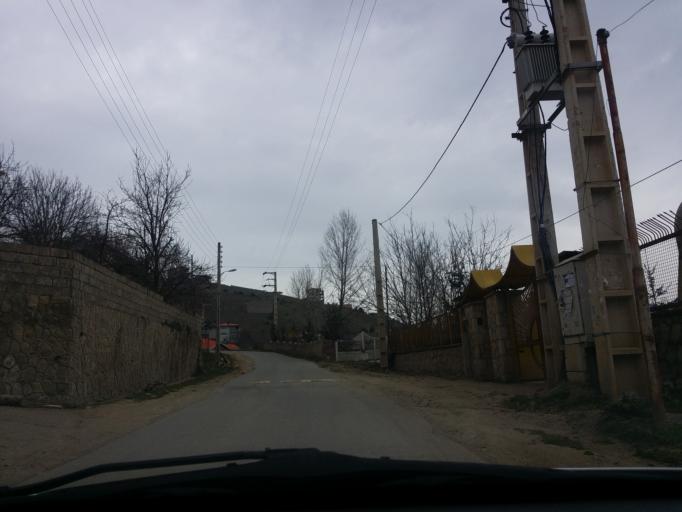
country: IR
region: Mazandaran
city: `Abbasabad
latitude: 36.5331
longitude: 51.1613
